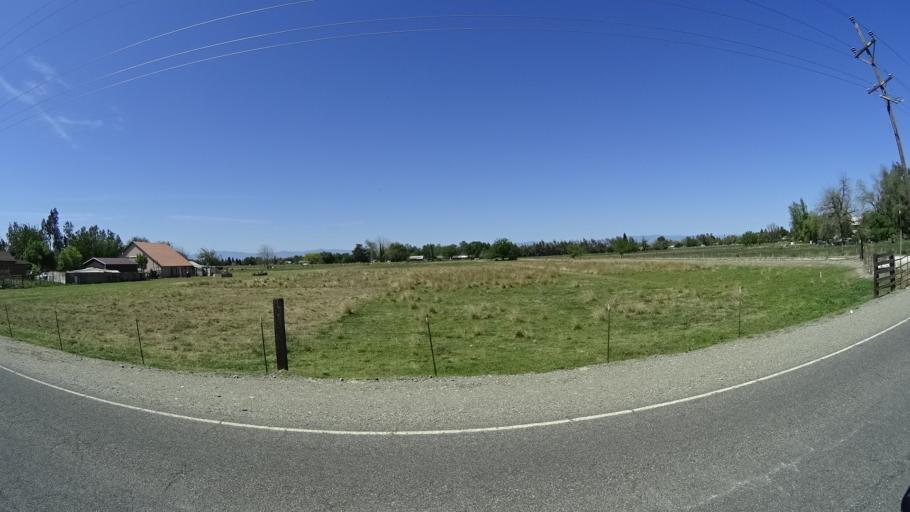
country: US
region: California
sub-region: Glenn County
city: Orland
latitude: 39.7324
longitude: -122.1781
